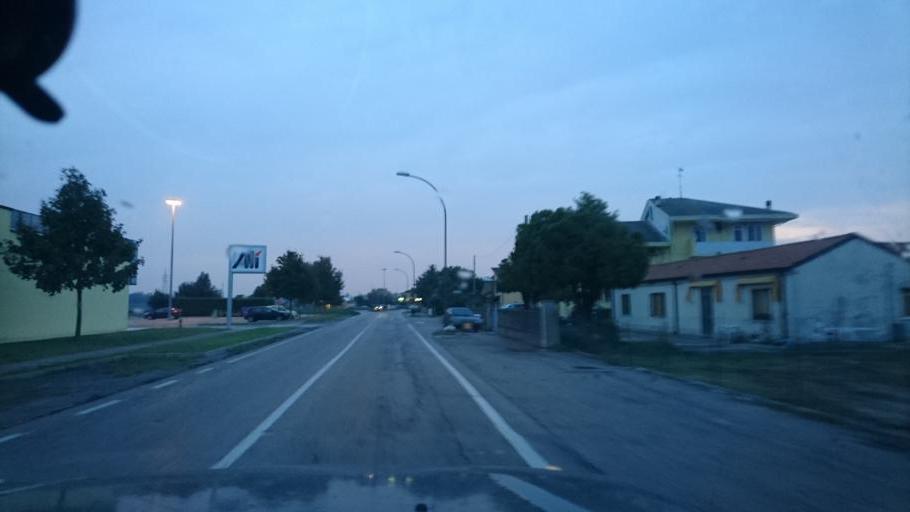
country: IT
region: Veneto
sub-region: Provincia di Rovigo
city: Porto Tolle
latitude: 44.9489
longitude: 12.3117
